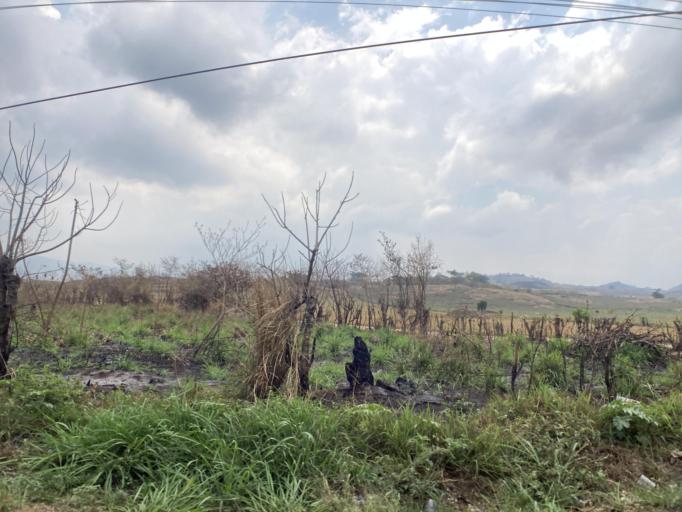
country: GT
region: Guatemala
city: Fraijanes
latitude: 14.3797
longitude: -90.4896
